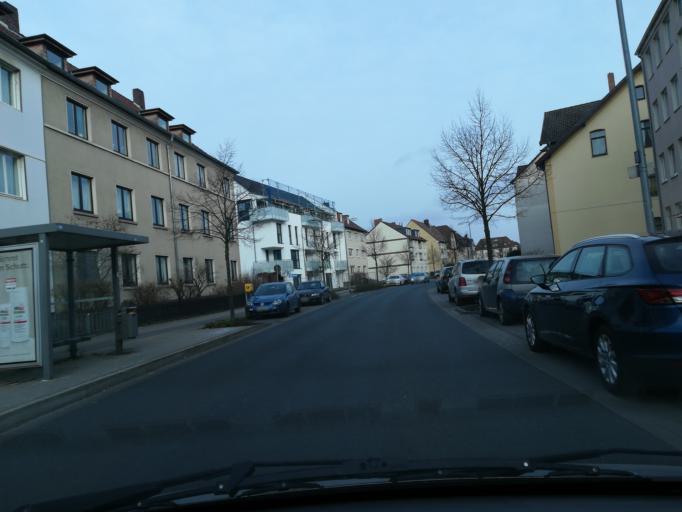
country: DE
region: Lower Saxony
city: Seelze
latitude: 52.3945
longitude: 9.6286
